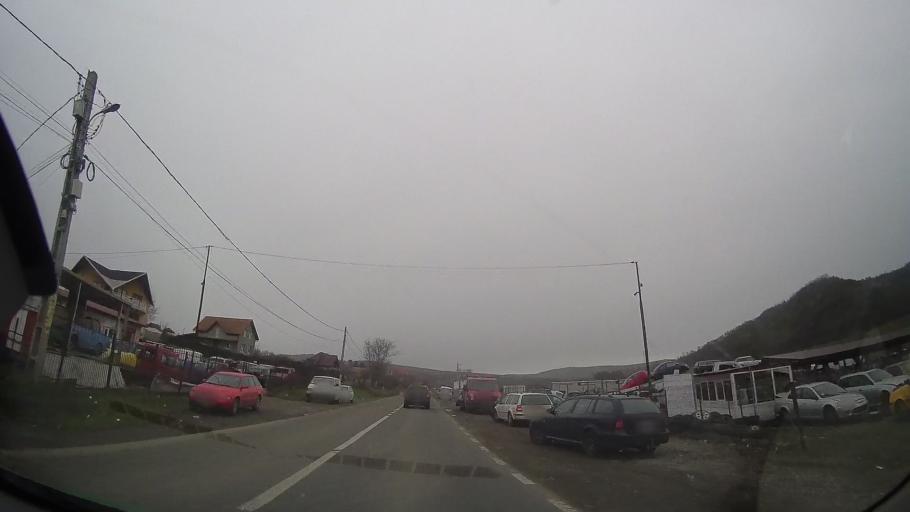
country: RO
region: Mures
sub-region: Comuna Ceausu de Campie
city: Ceausu de Campie
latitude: 46.6320
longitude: 24.5187
